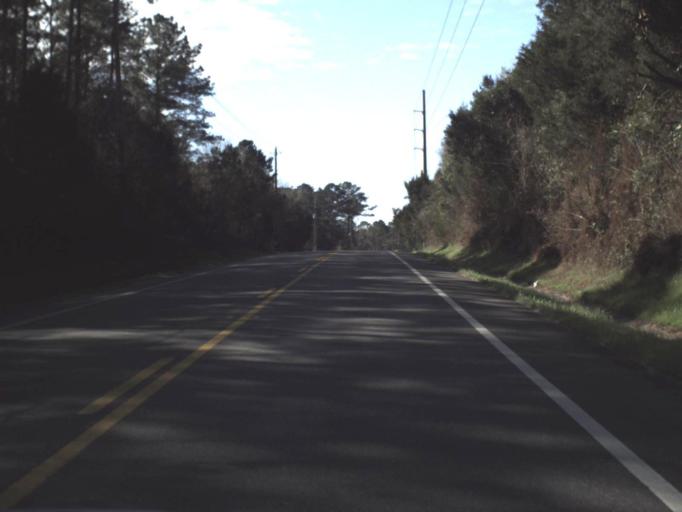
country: US
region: Florida
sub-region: Jackson County
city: Marianna
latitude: 30.7900
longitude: -85.1847
